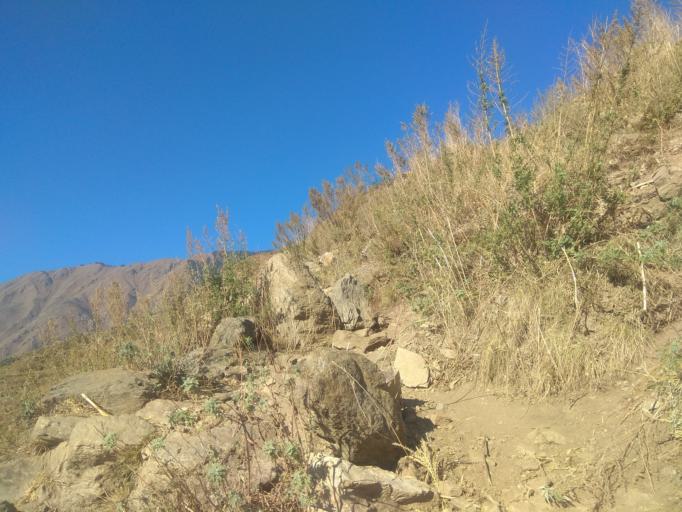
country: NP
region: Mid Western
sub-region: Bheri Zone
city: Dailekh
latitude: 29.2878
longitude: 81.7111
